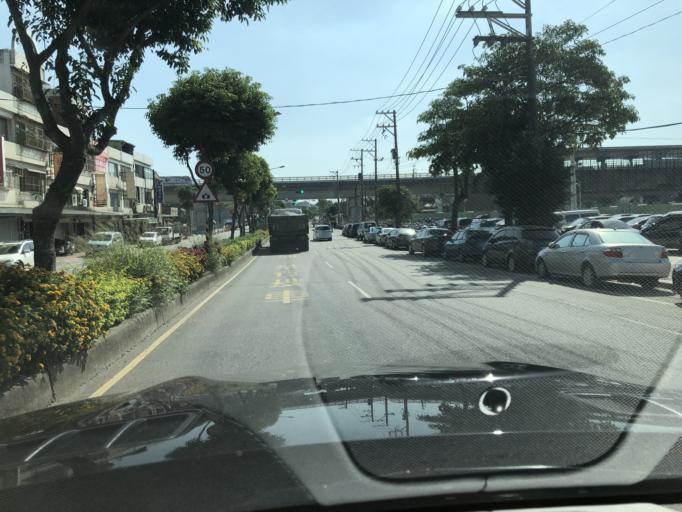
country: TW
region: Taiwan
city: Taoyuan City
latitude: 25.0822
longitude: 121.2859
